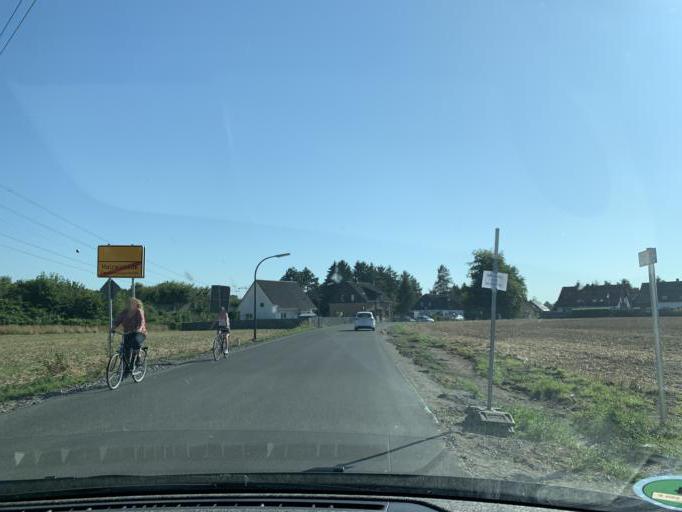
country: DE
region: North Rhine-Westphalia
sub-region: Regierungsbezirk Arnsberg
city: Holzwickede
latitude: 51.4808
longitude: 7.6098
